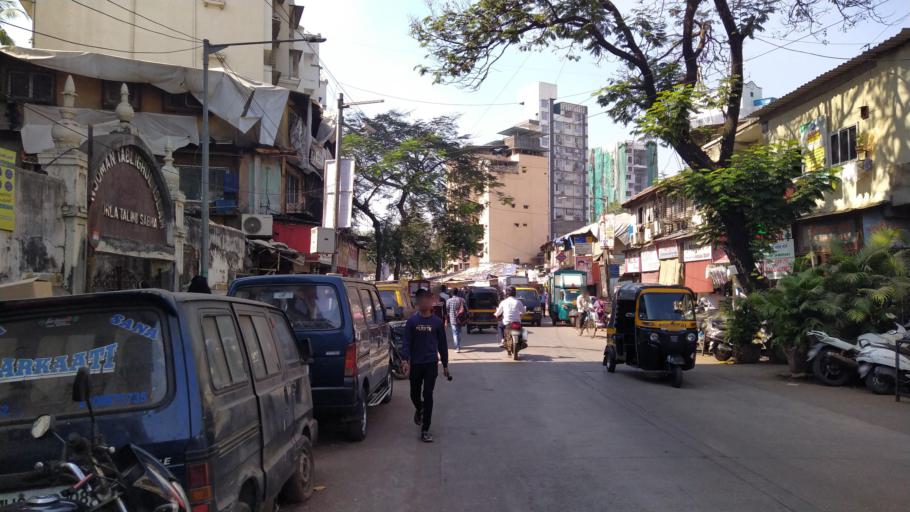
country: IN
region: Maharashtra
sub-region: Mumbai Suburban
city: Mumbai
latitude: 19.0656
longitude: 72.8763
